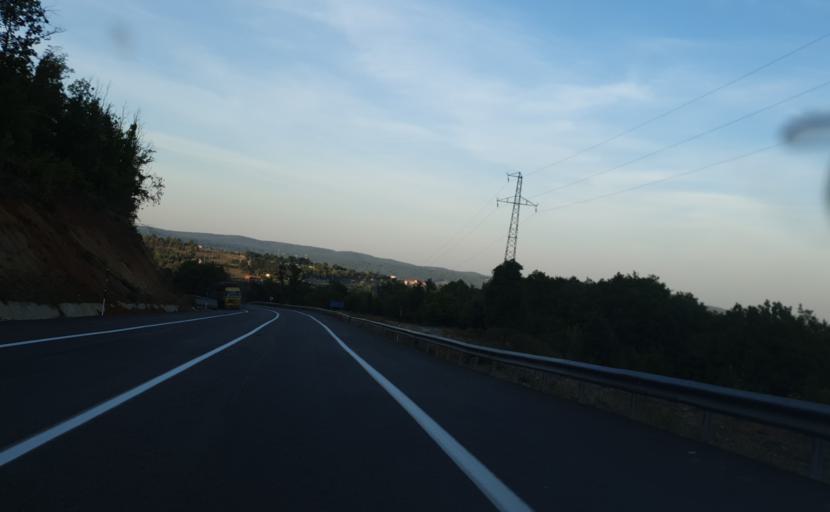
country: TR
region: Kirklareli
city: Sergen
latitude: 41.8114
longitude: 27.7487
